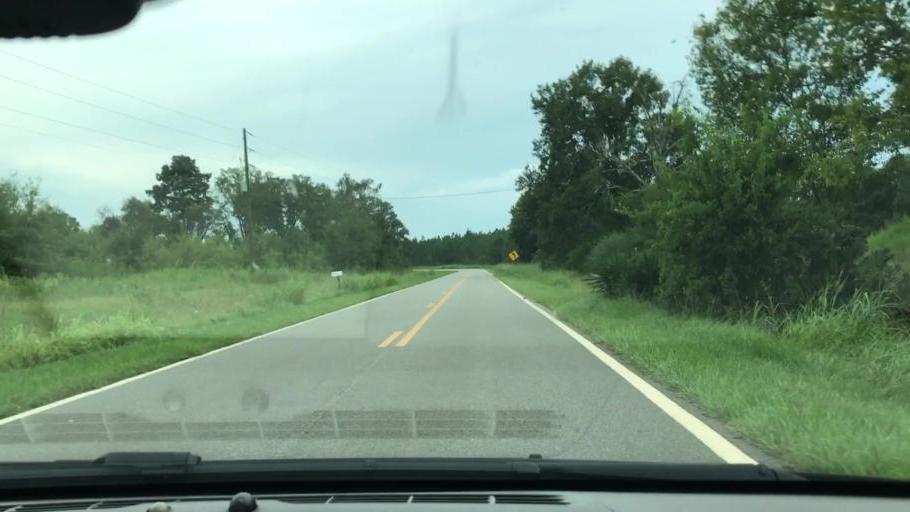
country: US
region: Georgia
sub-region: Early County
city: Blakely
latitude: 31.4299
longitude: -84.9233
